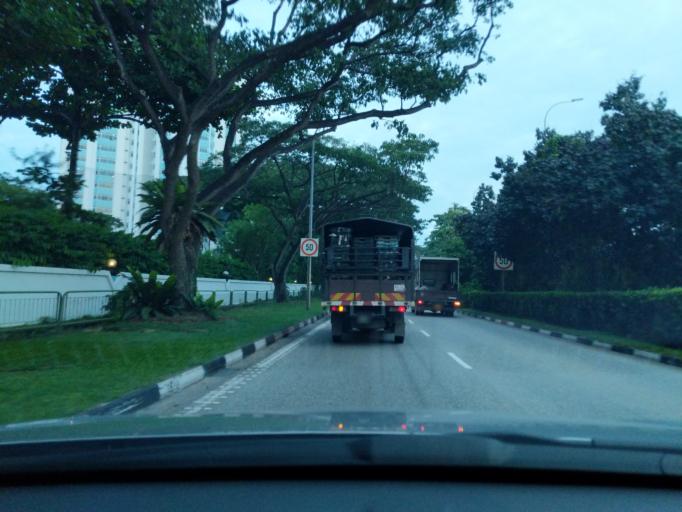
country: SG
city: Singapore
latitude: 1.2960
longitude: 103.8831
